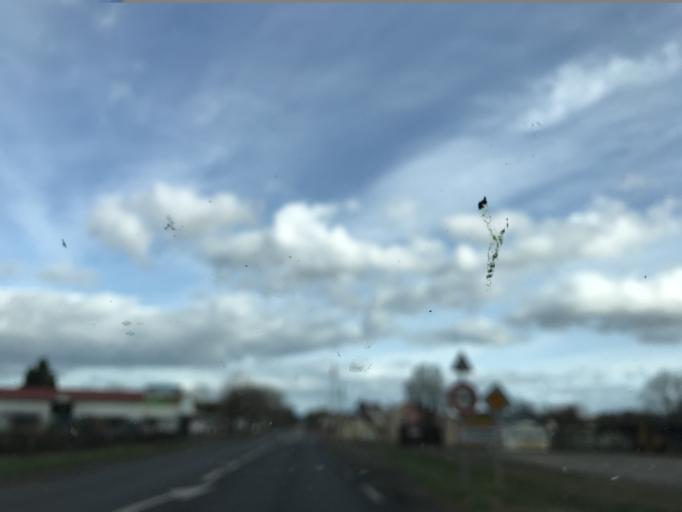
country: FR
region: Auvergne
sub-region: Departement du Puy-de-Dome
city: Vertaizon
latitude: 45.7857
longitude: 3.2762
